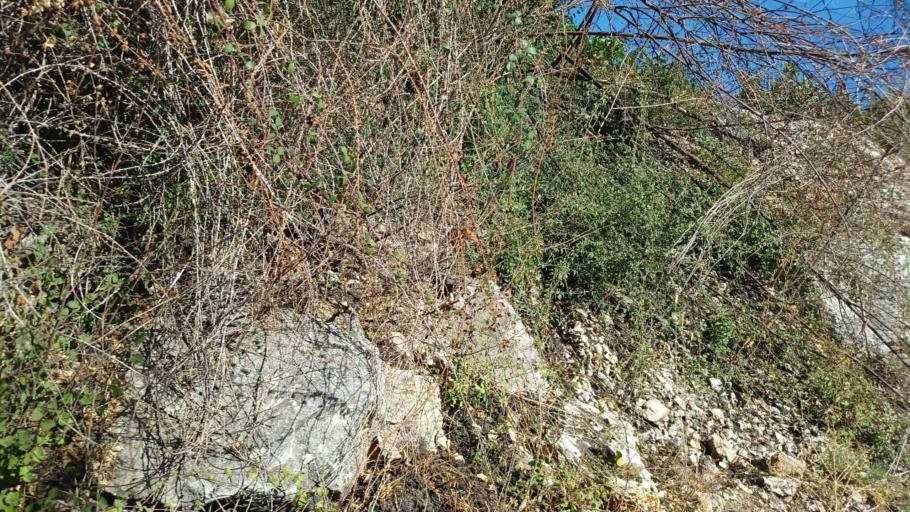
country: CY
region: Limassol
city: Pachna
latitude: 34.9012
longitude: 32.6440
